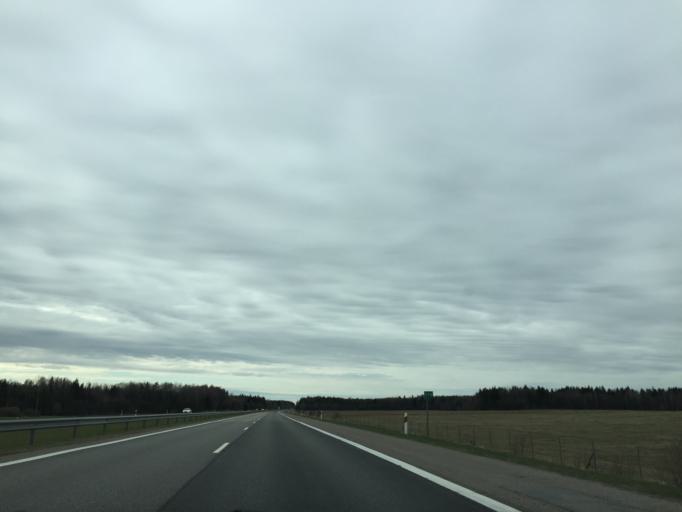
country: LT
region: Klaipedos apskritis
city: Gargzdai
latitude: 55.6974
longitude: 21.6420
